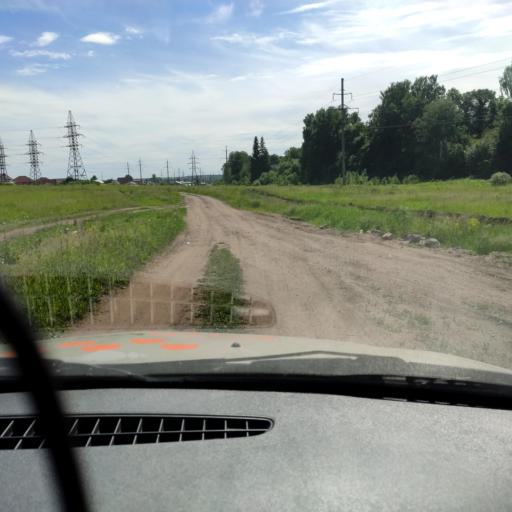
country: RU
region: Bashkortostan
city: Ufa
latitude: 54.6838
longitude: 56.0869
